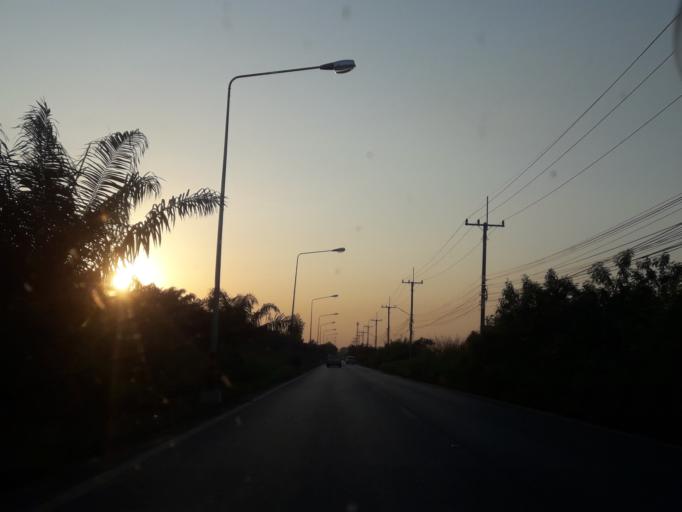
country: TH
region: Pathum Thani
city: Nong Suea
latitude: 14.1313
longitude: 100.7888
